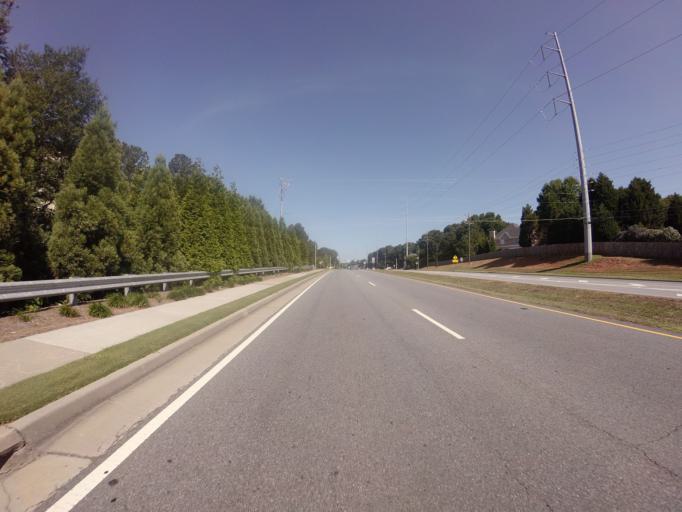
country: US
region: Georgia
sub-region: Gwinnett County
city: Duluth
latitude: 34.0565
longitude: -84.1469
